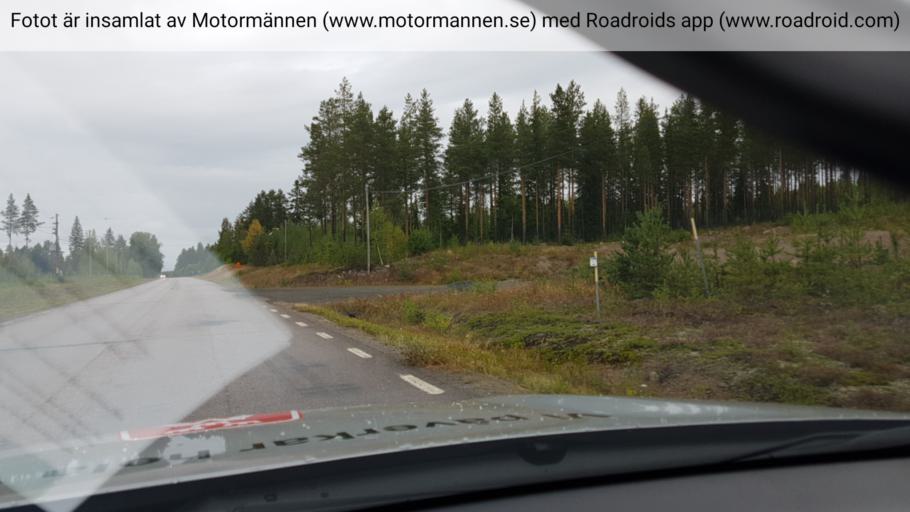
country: SE
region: Norrbotten
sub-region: Alvsbyns Kommun
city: AElvsbyn
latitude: 66.1061
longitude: 20.9353
